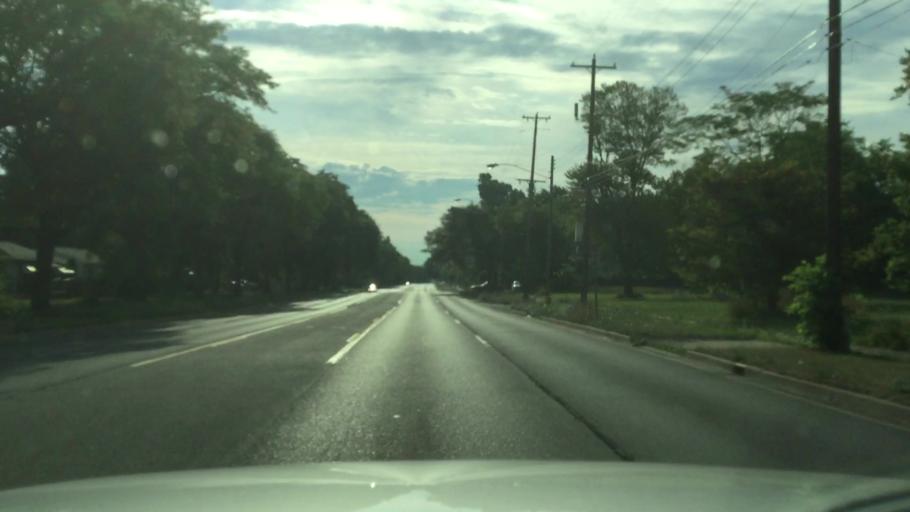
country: US
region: Michigan
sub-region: Genesee County
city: Beecher
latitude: 43.0607
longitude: -83.7224
